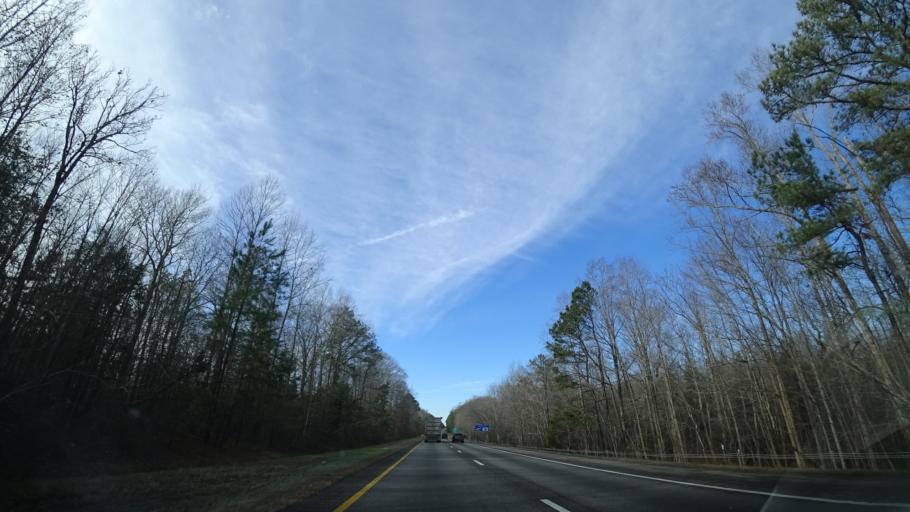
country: US
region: Virginia
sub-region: New Kent County
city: New Kent
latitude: 37.4992
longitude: -77.0605
